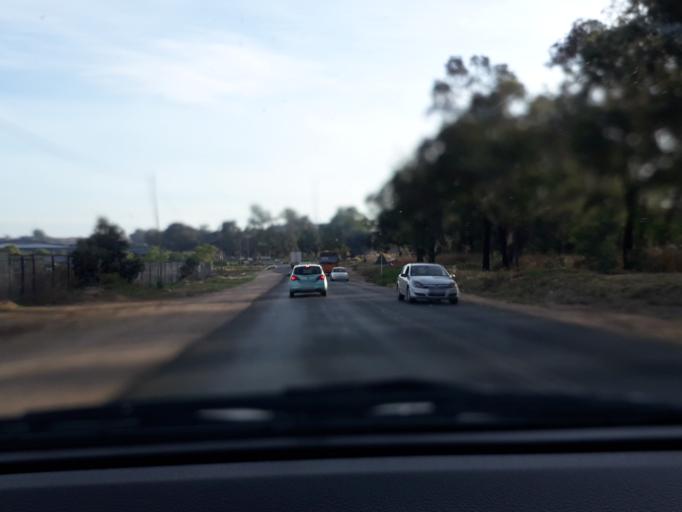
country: ZA
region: Gauteng
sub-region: City of Tshwane Metropolitan Municipality
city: Centurion
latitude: -25.9182
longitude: 28.1554
